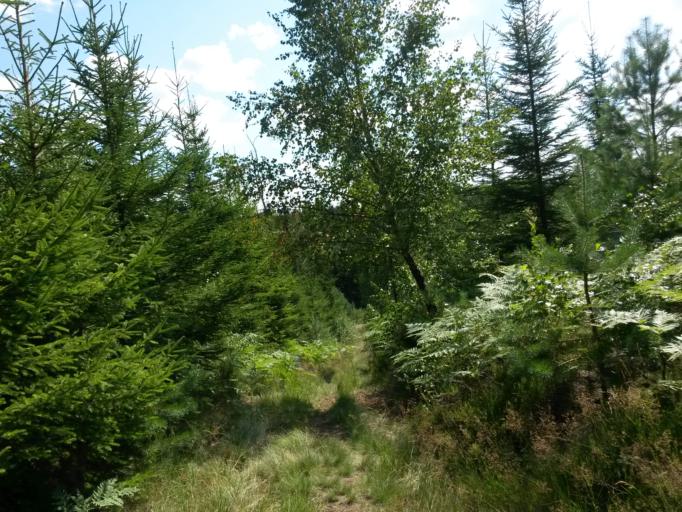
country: SE
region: Vaestra Goetaland
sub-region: Vargarda Kommun
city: Jonstorp
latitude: 57.9544
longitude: 12.6869
